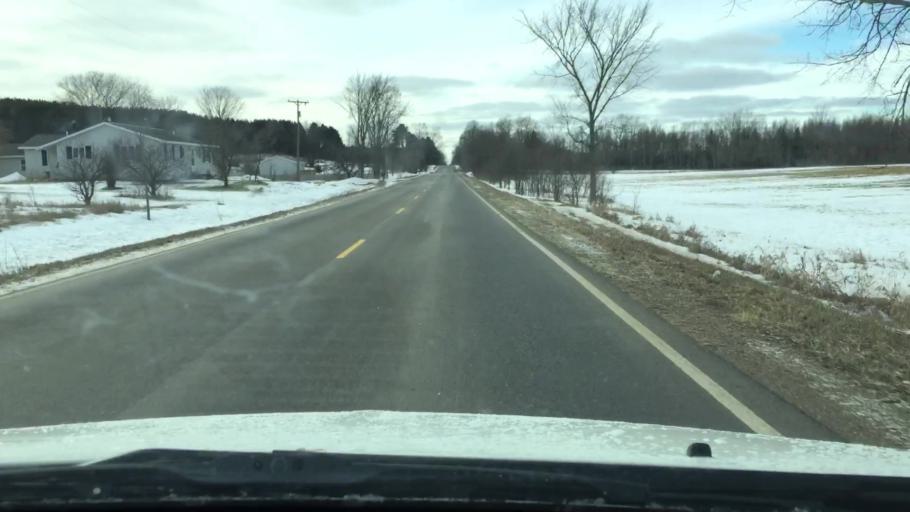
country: US
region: Michigan
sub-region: Wexford County
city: Manton
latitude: 44.4036
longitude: -85.4237
